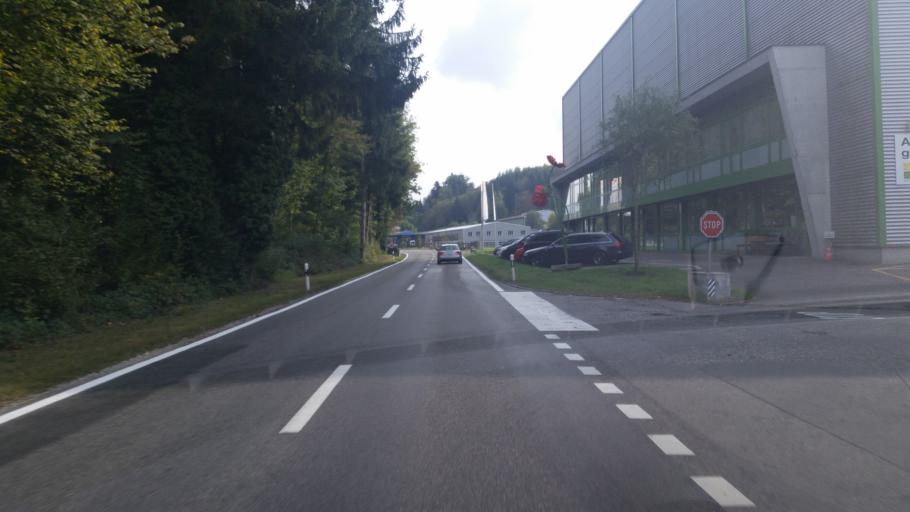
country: CH
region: Aargau
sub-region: Bezirk Bremgarten
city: Bremgarten
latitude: 47.3594
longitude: 8.3204
